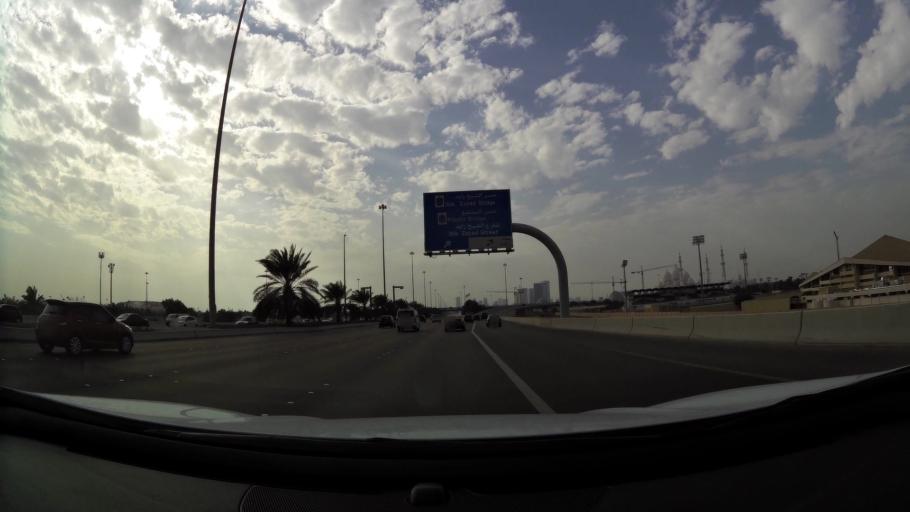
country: AE
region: Abu Dhabi
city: Abu Dhabi
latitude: 24.4047
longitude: 54.4822
